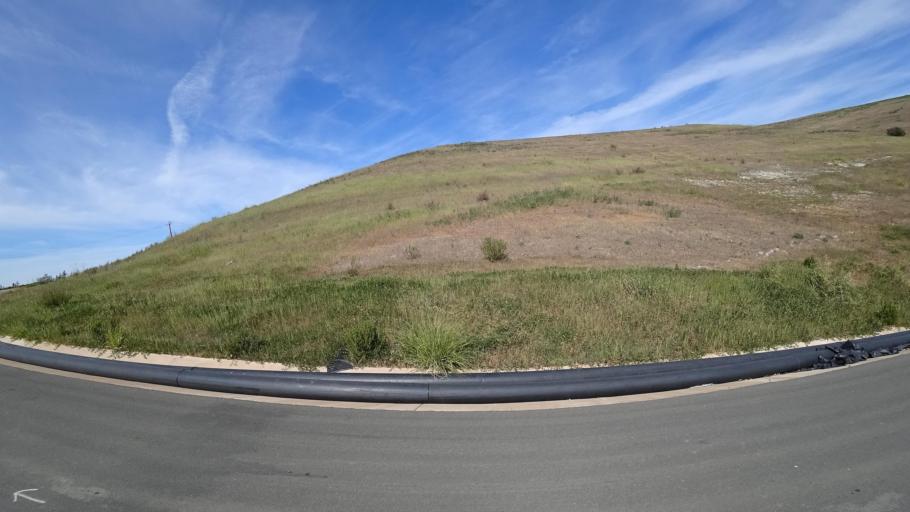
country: US
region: California
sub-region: Alameda County
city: Fairview
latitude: 37.6371
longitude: -122.0510
